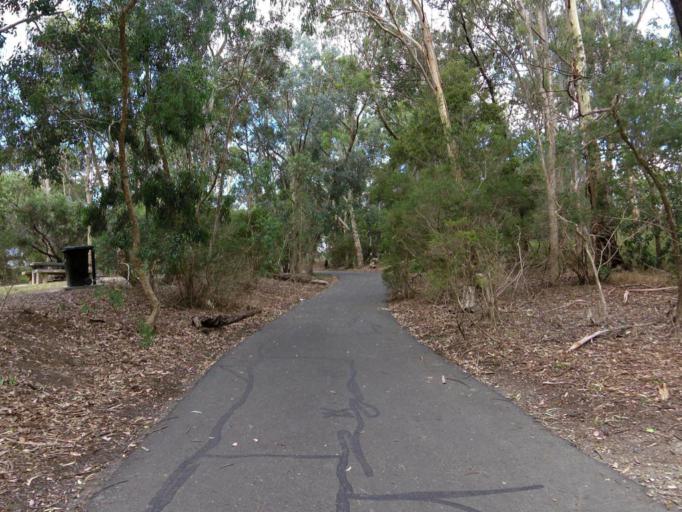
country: AU
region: Victoria
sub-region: Maroondah
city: Ringwood East
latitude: -37.8138
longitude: 145.2405
